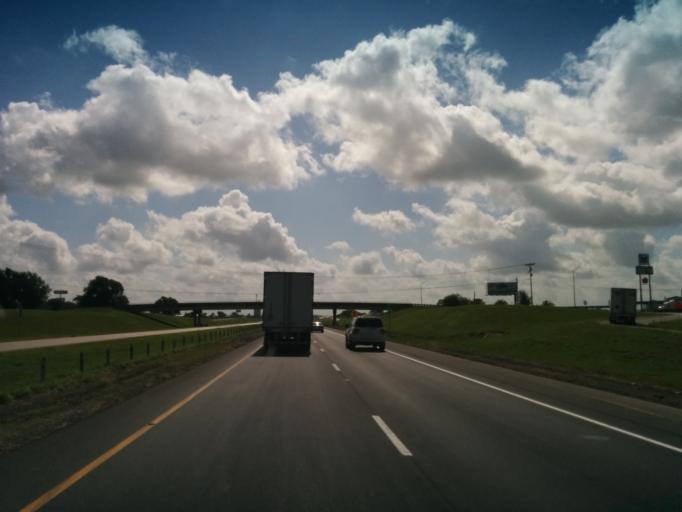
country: US
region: Texas
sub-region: Colorado County
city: Weimar
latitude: 29.6916
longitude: -96.7781
